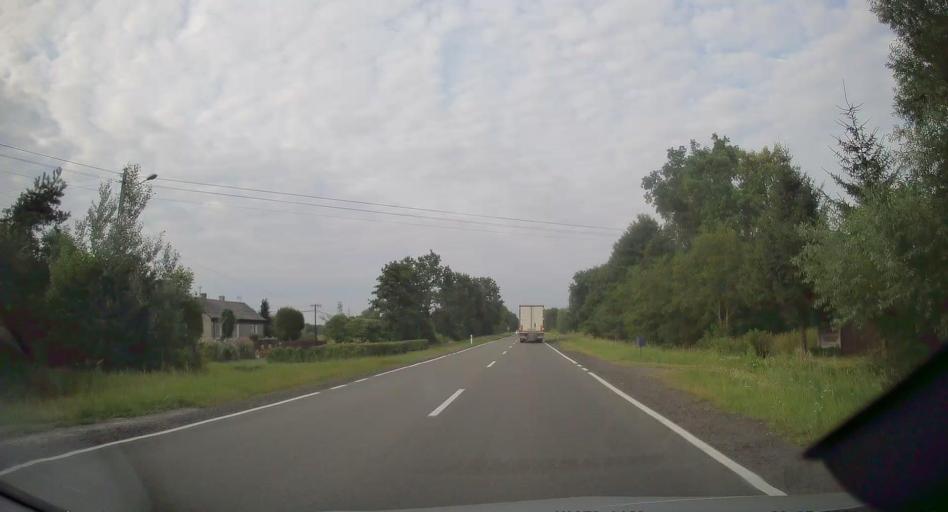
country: PL
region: Silesian Voivodeship
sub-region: Powiat czestochowski
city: Klomnice
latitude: 50.9338
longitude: 19.3829
